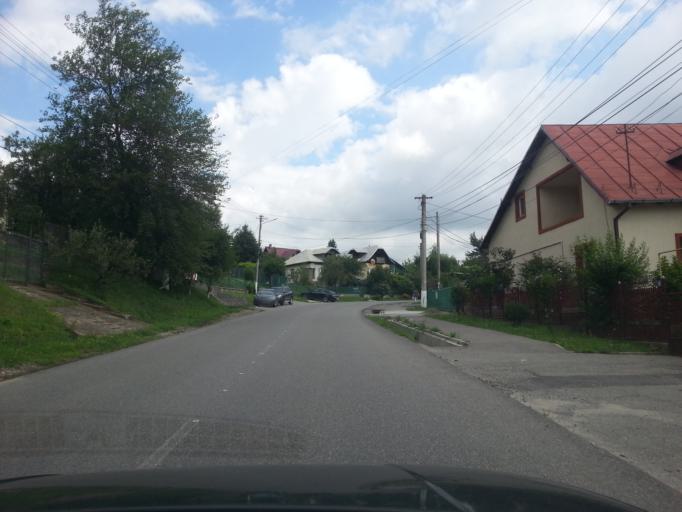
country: RO
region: Prahova
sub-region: Comuna Cornu
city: Cornu de Jos
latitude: 45.1548
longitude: 25.6886
